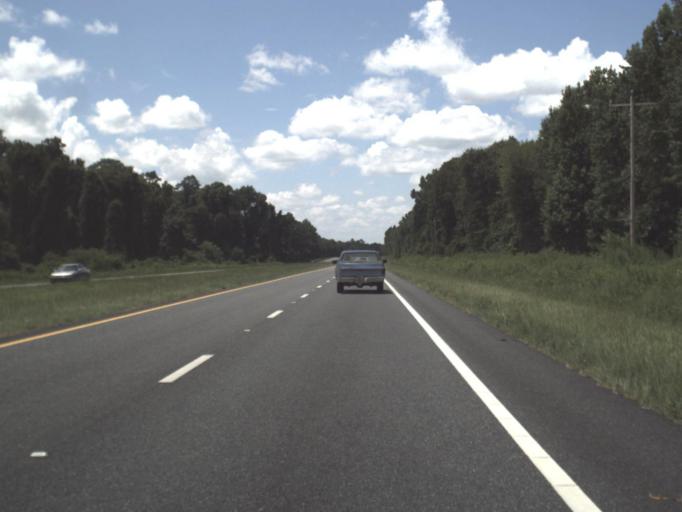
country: US
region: Florida
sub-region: Jefferson County
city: Monticello
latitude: 30.3314
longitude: -83.7756
